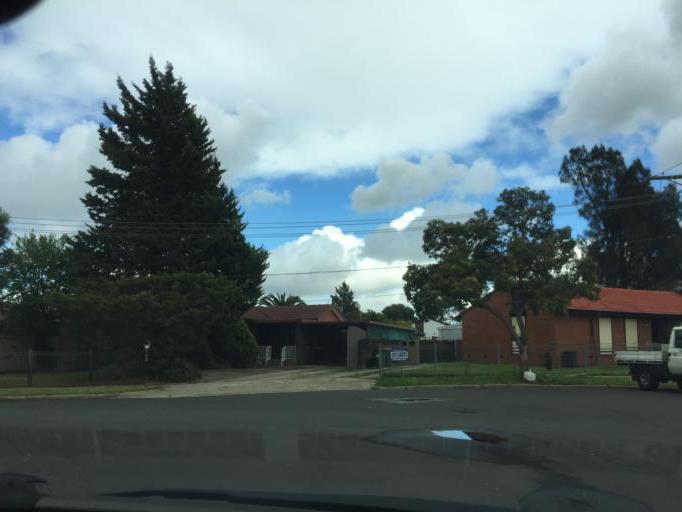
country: AU
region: Victoria
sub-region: Brimbank
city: Sunshine West
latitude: -37.8029
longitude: 144.8231
